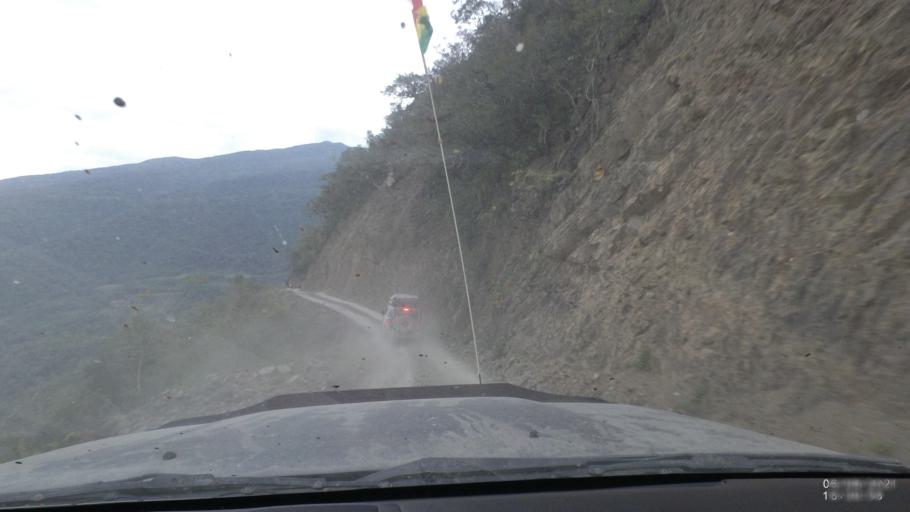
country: BO
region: La Paz
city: Quime
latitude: -16.5183
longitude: -66.7695
